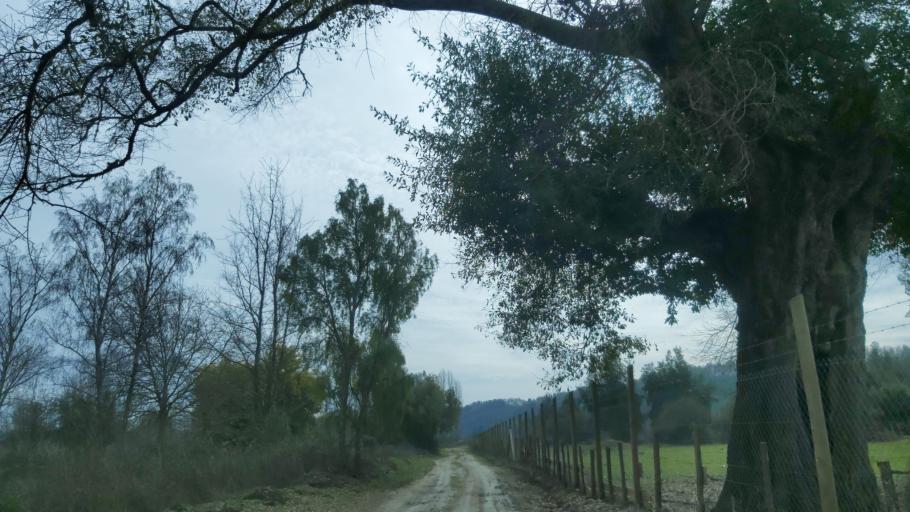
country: CL
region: Biobio
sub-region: Provincia de Nuble
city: Coihueco
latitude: -36.3910
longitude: -71.5738
